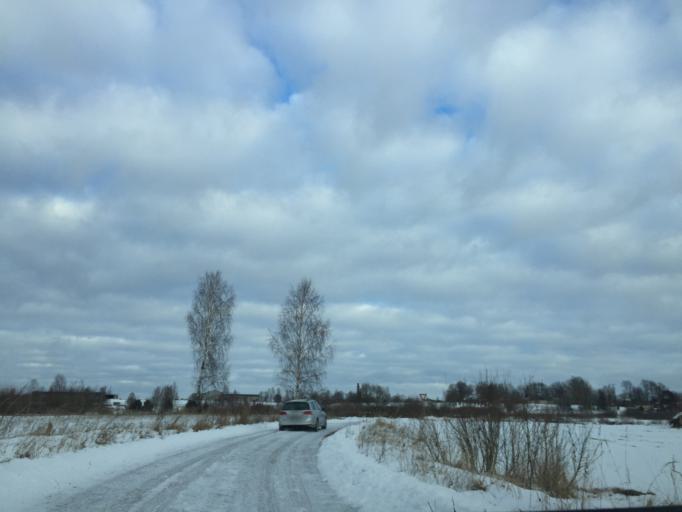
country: LV
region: Lielvarde
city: Lielvarde
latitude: 56.6261
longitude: 24.7407
